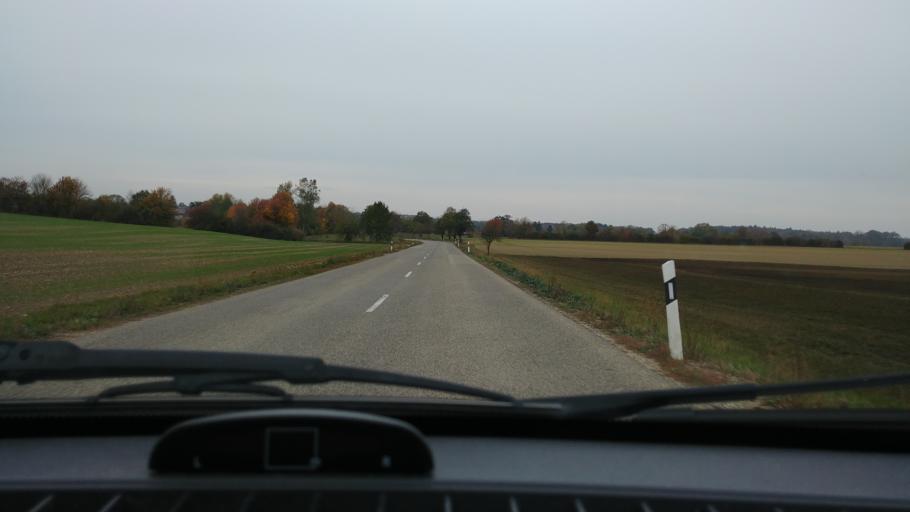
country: DE
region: Baden-Wuerttemberg
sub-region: Regierungsbezirk Stuttgart
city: Schrozberg
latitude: 49.3408
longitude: 10.0408
